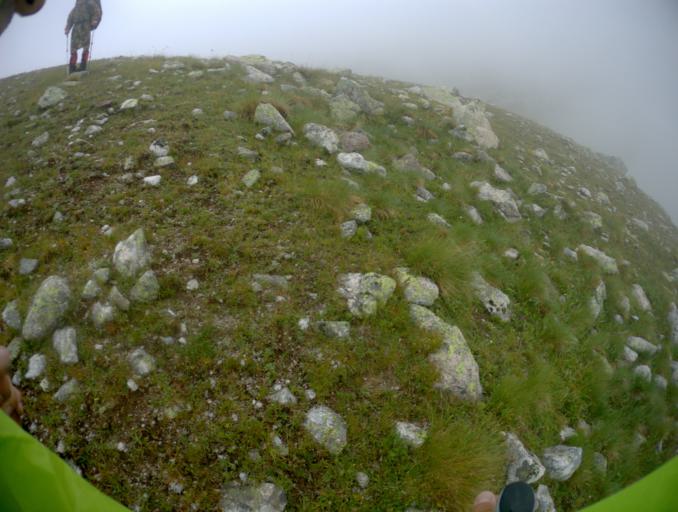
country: RU
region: Karachayevo-Cherkesiya
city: Uchkulan
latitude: 43.2859
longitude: 42.0988
